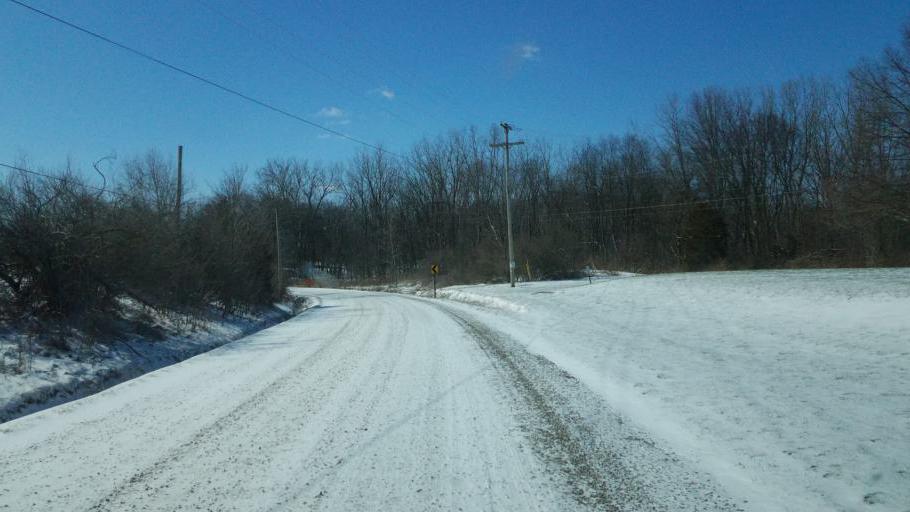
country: US
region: Ohio
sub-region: Morrow County
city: Mount Gilead
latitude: 40.4937
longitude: -82.7181
